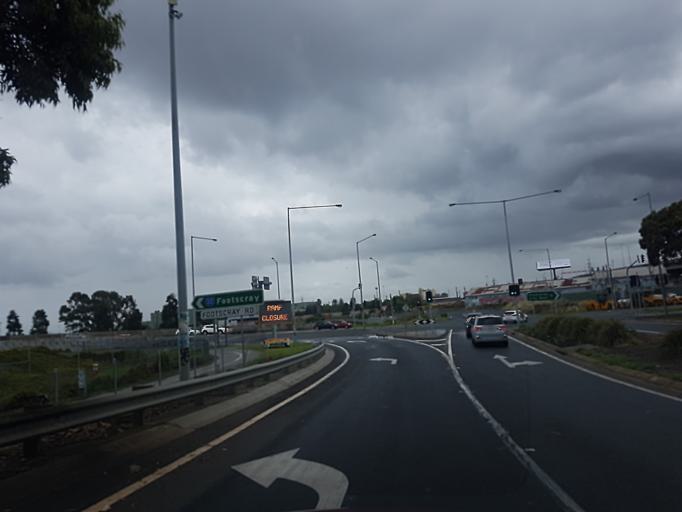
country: AU
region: Victoria
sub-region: Melbourne
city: North Melbourne
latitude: -37.8099
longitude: 144.9319
